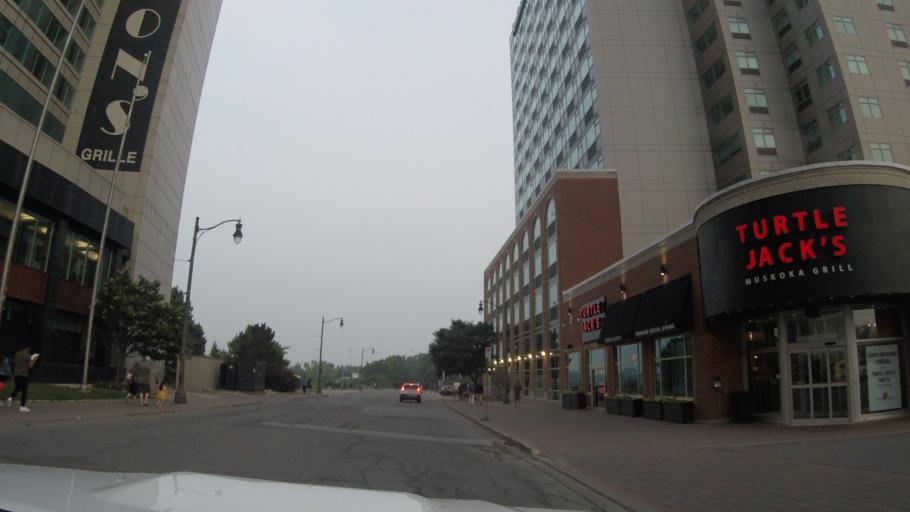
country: CA
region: Ontario
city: Niagara Falls
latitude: 43.0787
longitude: -79.0823
